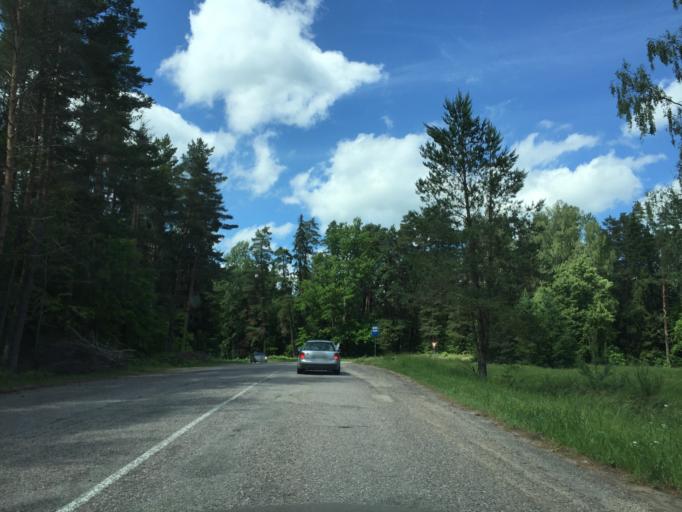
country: LV
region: Engure
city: Smarde
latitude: 56.9833
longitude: 23.2802
